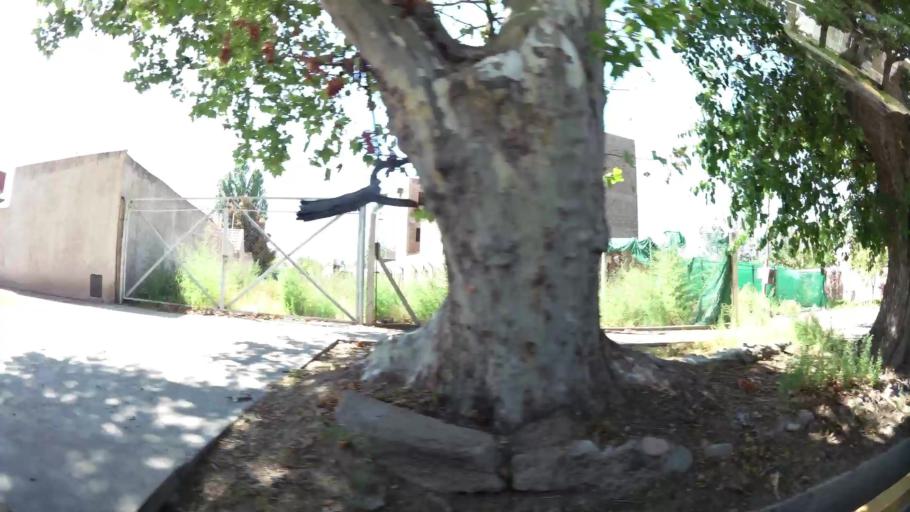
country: AR
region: Mendoza
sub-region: Departamento de Godoy Cruz
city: Godoy Cruz
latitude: -32.9495
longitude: -68.8405
